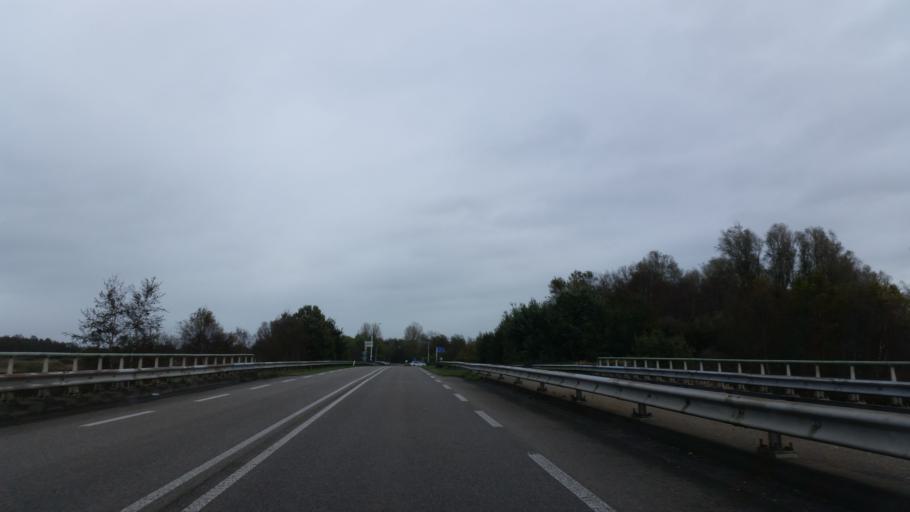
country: NL
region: Friesland
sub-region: Gemeente Skarsterlan
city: Sint Nicolaasga
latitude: 52.9145
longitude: 5.7745
